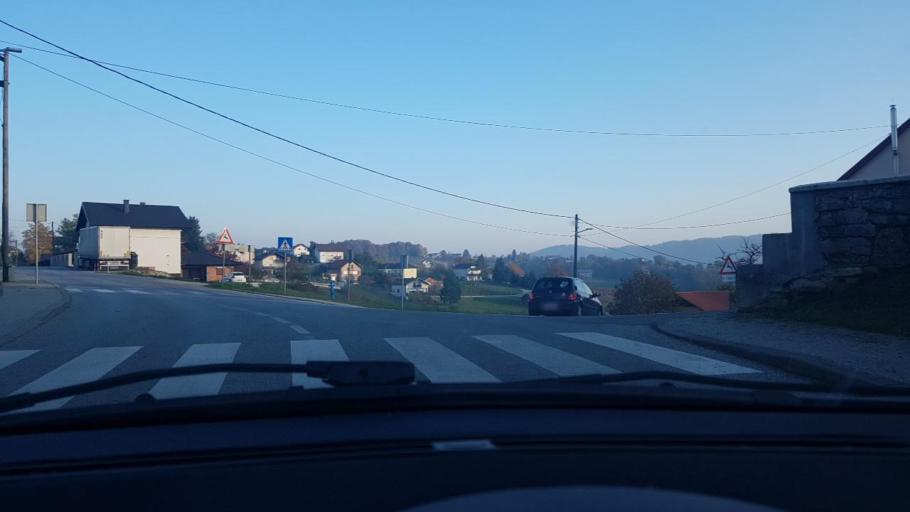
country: SI
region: Rogatec
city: Rogatec
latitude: 46.2136
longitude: 15.6739
